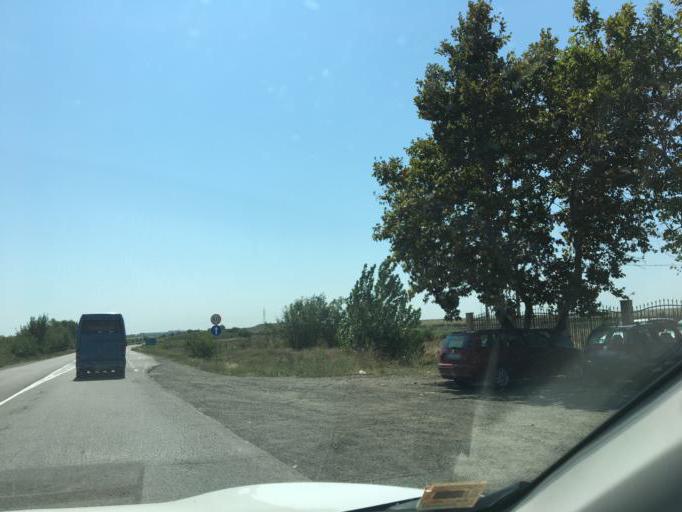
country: BG
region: Burgas
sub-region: Obshtina Kameno
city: Kameno
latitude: 42.5981
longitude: 27.3901
